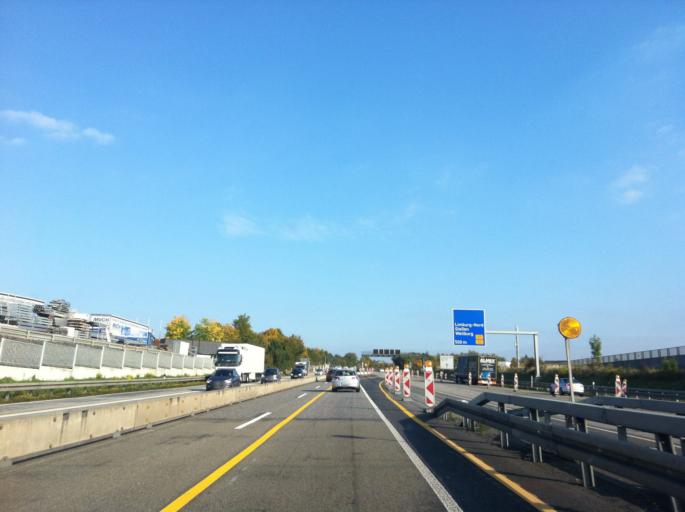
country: DE
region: Rheinland-Pfalz
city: Eppenrod
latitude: 50.4126
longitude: 7.9362
